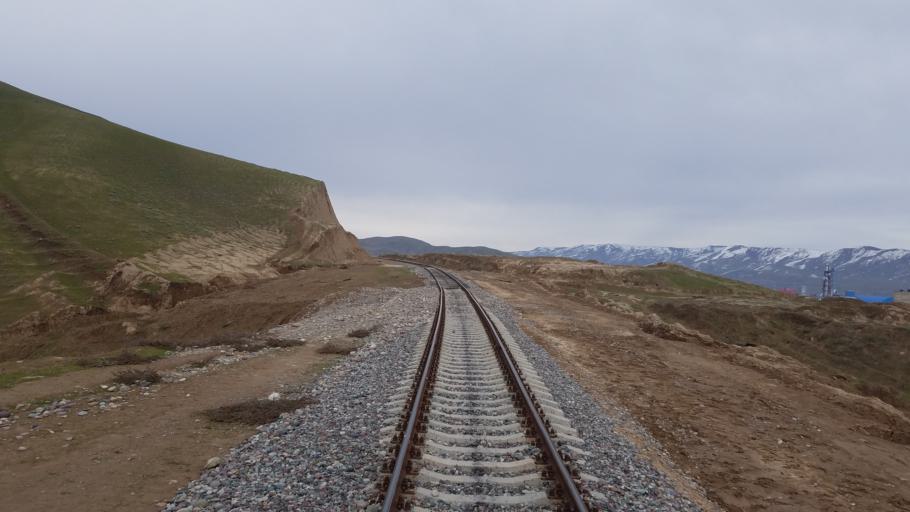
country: TJ
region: Khatlon
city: Yovon
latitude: 38.3243
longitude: 68.9642
